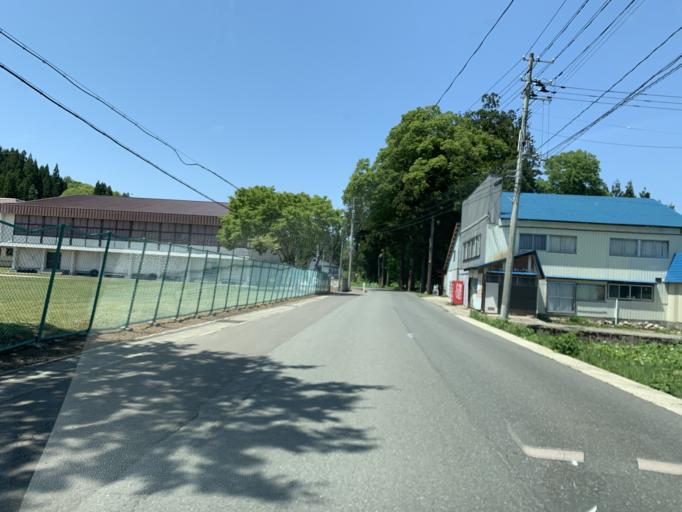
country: JP
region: Akita
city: Yokotemachi
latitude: 39.3542
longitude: 140.7680
